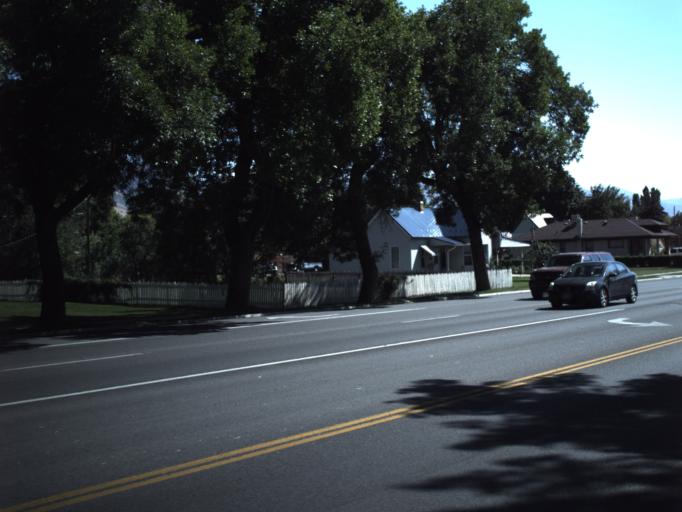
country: US
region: Utah
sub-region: Cache County
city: Smithfield
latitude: 41.8427
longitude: -111.8326
